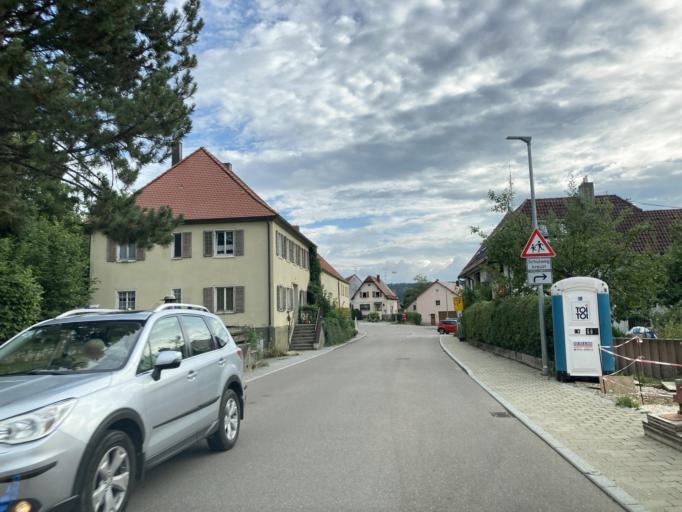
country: DE
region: Baden-Wuerttemberg
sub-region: Regierungsbezirk Stuttgart
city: Dischingen
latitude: 48.6967
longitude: 10.3643
